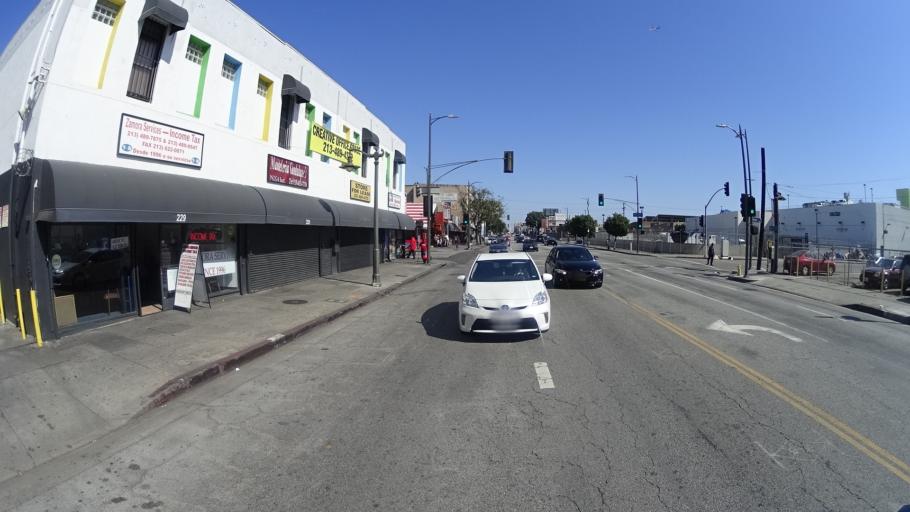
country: US
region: California
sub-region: Los Angeles County
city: Los Angeles
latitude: 34.0427
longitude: -118.2496
